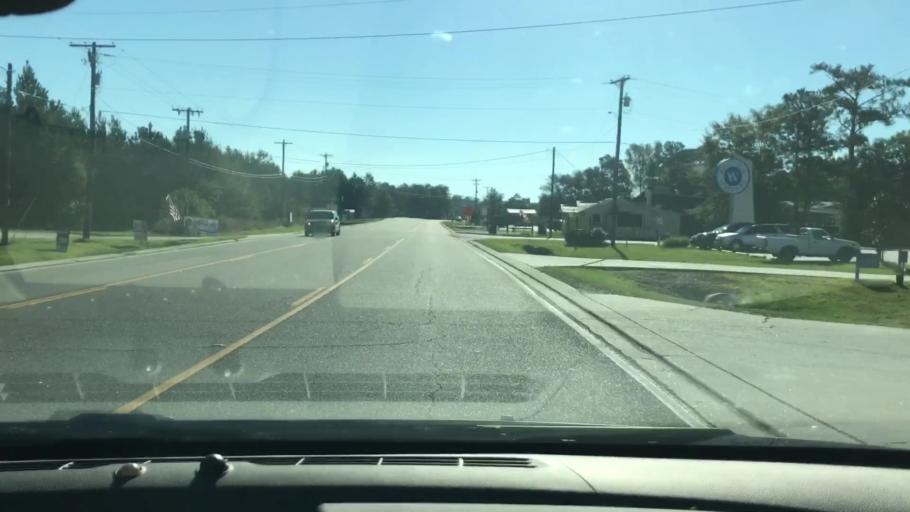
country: US
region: Louisiana
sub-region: Saint Tammany Parish
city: Pearl River
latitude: 30.3634
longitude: -89.7552
